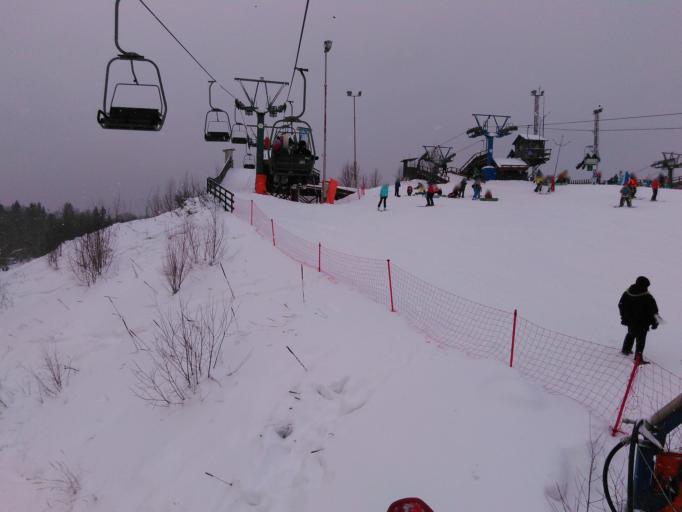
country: RU
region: Moskovskaya
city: Yakhroma
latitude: 56.2595
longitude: 37.4319
